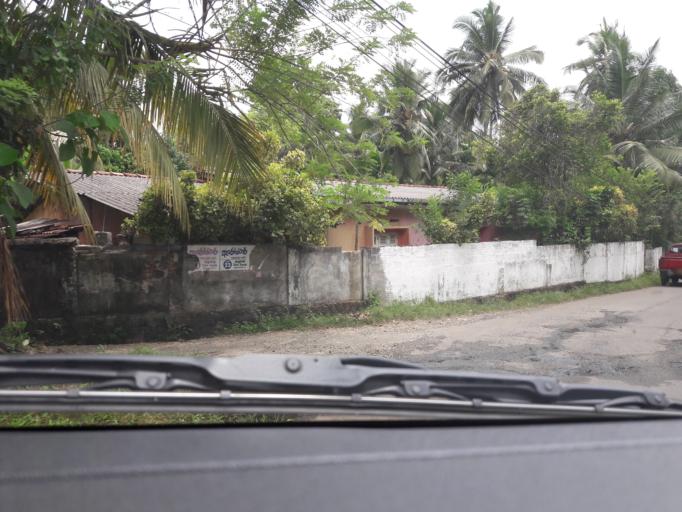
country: LK
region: Southern
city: Unawatuna
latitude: 6.0498
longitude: 80.2497
